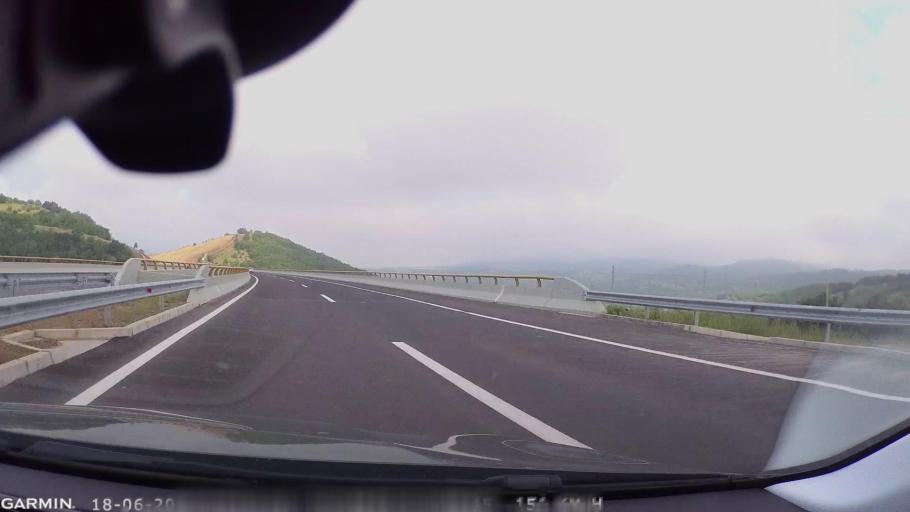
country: MK
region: Sveti Nikole
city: Gorobinci
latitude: 41.9209
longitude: 21.8649
